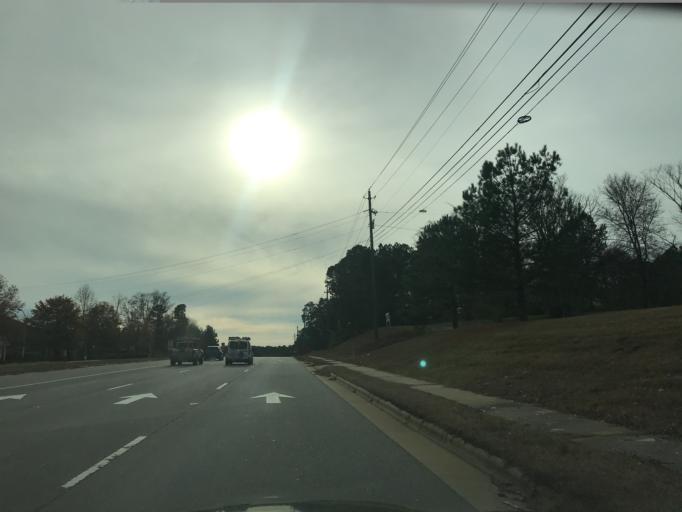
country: US
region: North Carolina
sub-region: Wake County
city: Knightdale
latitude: 35.8511
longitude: -78.5605
